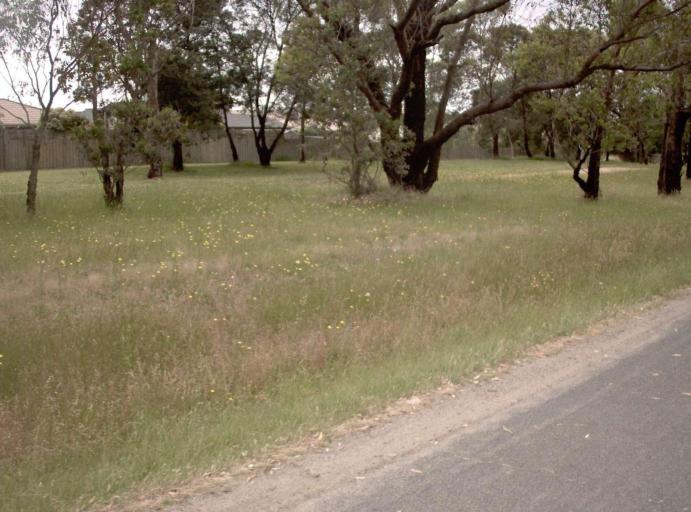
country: AU
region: Victoria
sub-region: Casey
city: Lynbrook
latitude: -38.0669
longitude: 145.2669
